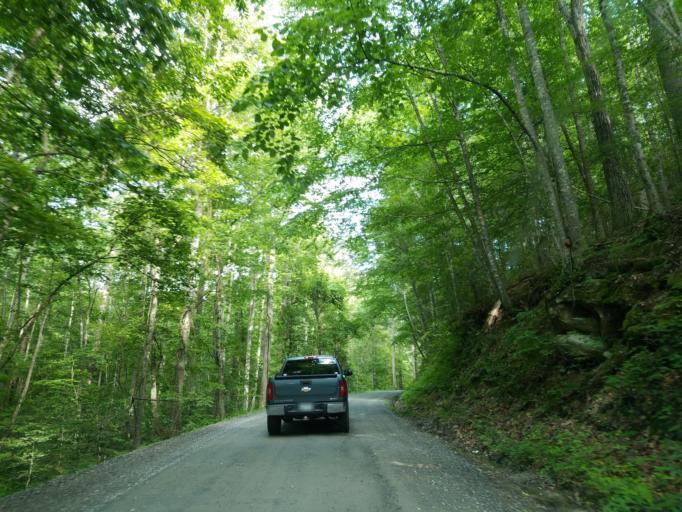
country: US
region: Georgia
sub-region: Fannin County
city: Blue Ridge
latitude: 34.7821
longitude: -84.2348
